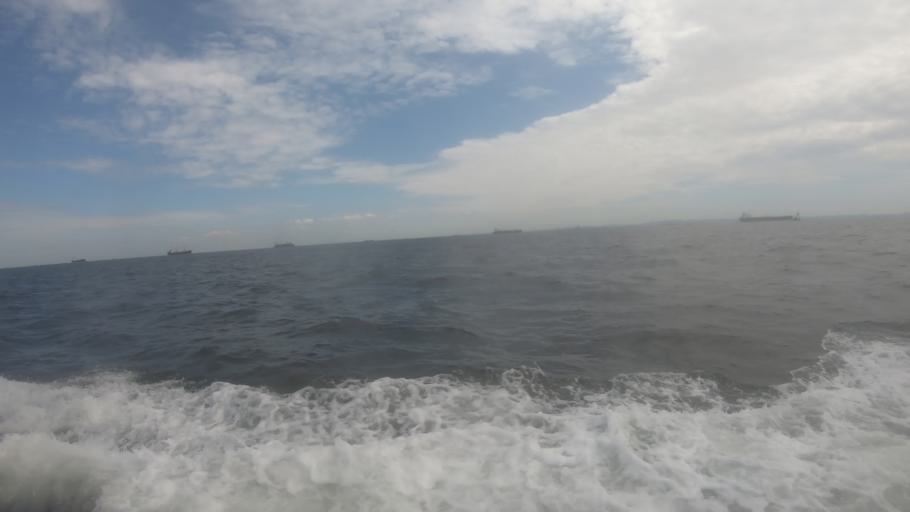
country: JP
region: Kanagawa
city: Yokohama
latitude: 35.4325
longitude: 139.6917
